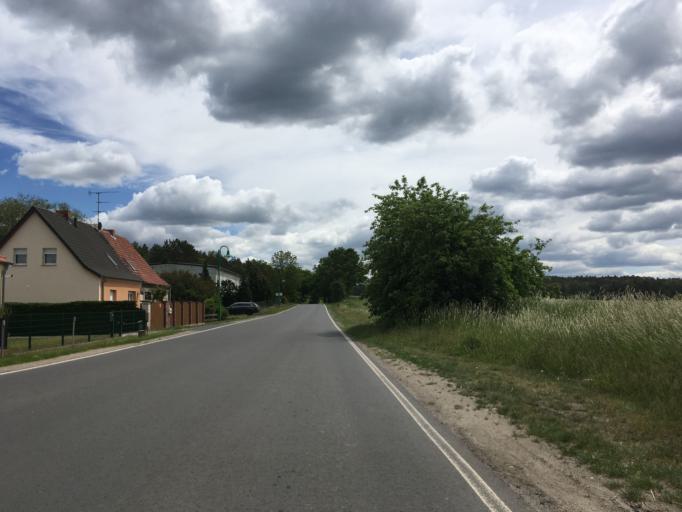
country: DE
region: Brandenburg
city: Falkenberg
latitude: 52.7706
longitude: 13.9575
